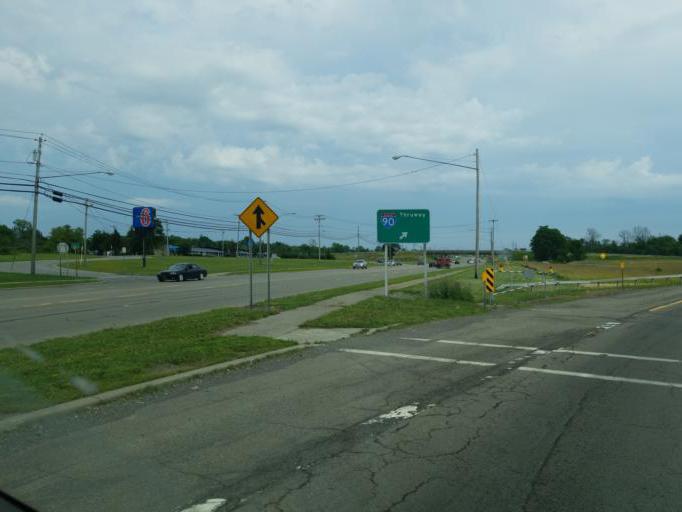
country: US
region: New York
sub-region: Erie County
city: Hamburg
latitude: 42.7451
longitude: -78.8511
